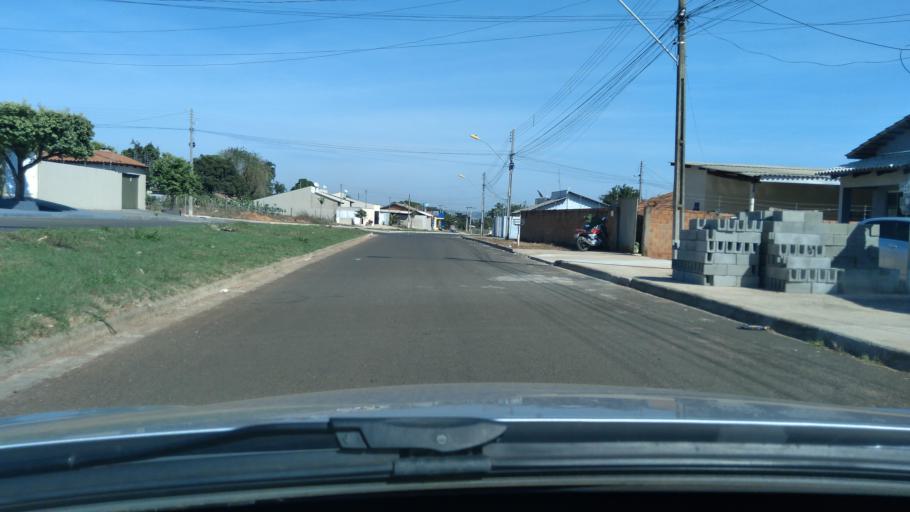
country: BR
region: Goias
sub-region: Mineiros
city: Mineiros
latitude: -17.5798
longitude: -52.5593
